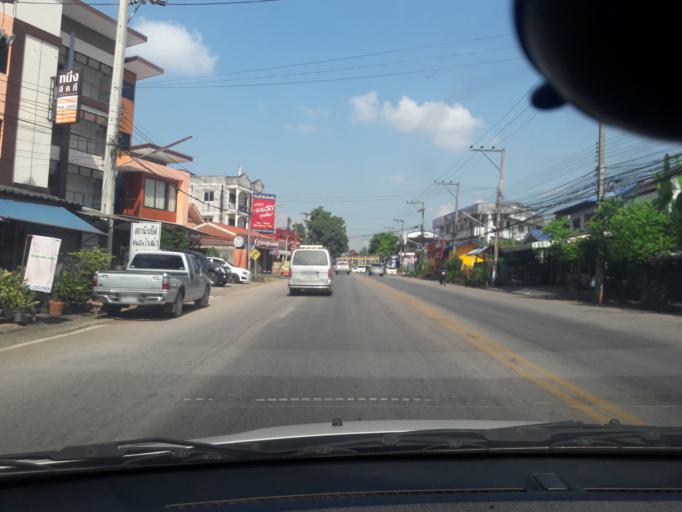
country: TH
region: Lampang
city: Lampang
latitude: 18.2483
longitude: 99.4907
